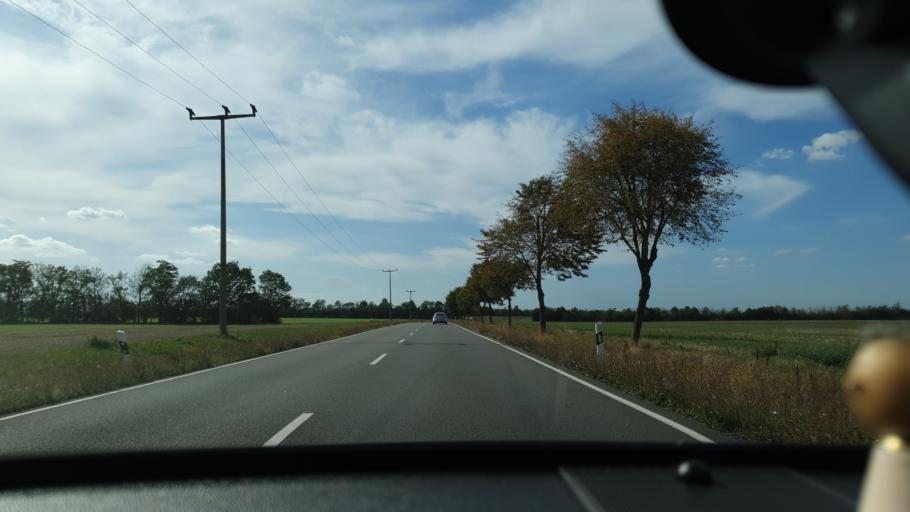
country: DE
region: Saxony
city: Jesewitz
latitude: 51.4563
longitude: 12.5588
